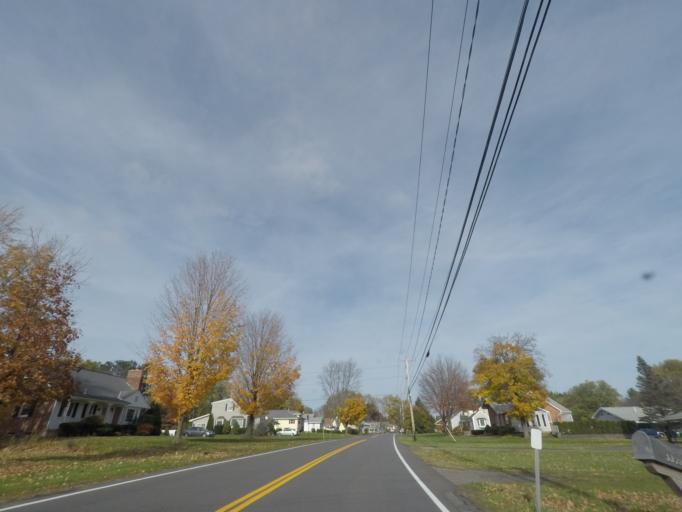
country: US
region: New York
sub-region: Schenectady County
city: Rotterdam
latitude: 42.7613
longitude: -73.9869
